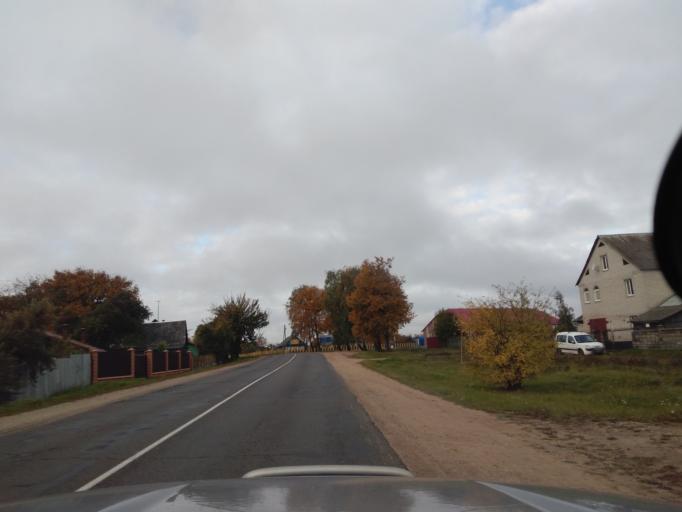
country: BY
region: Minsk
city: Kapyl'
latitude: 53.1604
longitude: 27.0805
